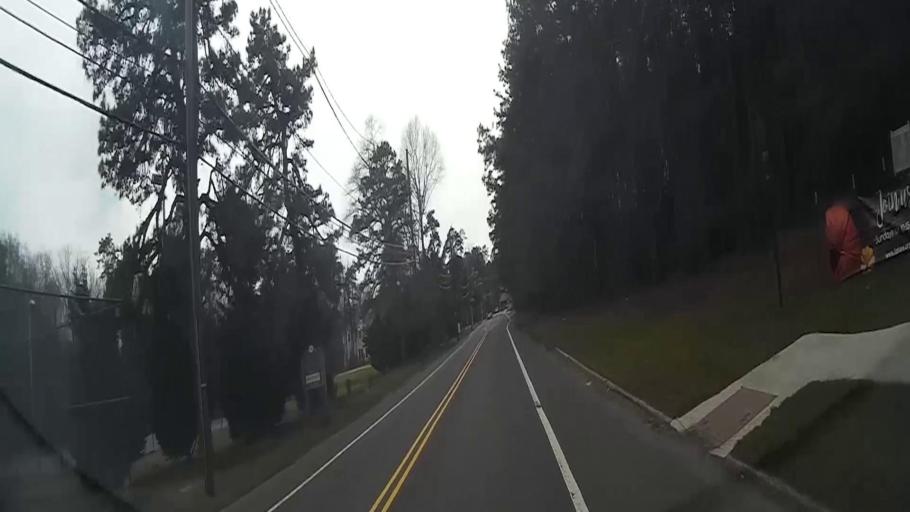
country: US
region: New Jersey
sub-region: Burlington County
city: Medford Lakes
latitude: 39.8559
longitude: -74.8559
